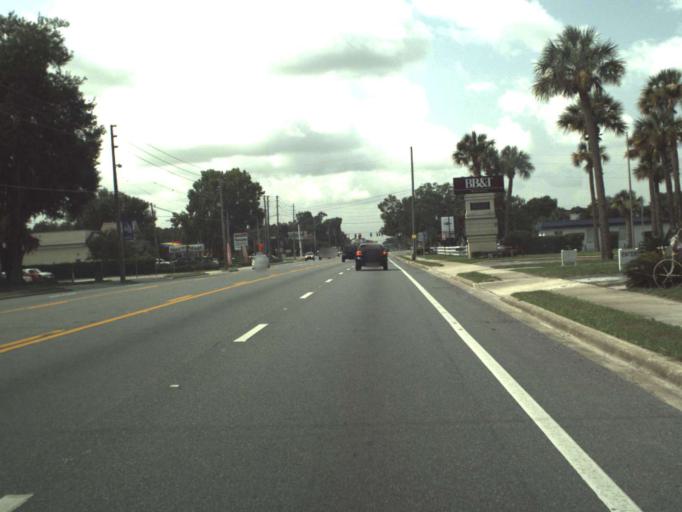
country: US
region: Florida
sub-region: Sumter County
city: Wildwood
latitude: 28.8502
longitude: -82.0455
